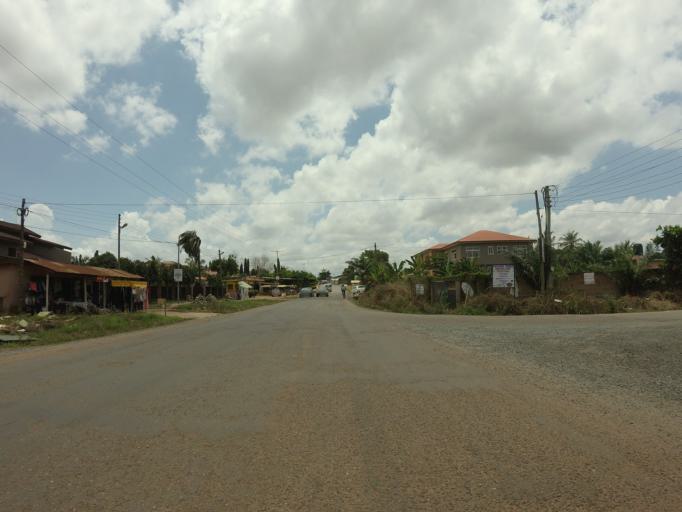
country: GH
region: Greater Accra
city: Medina Estates
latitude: 5.6810
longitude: -0.1969
